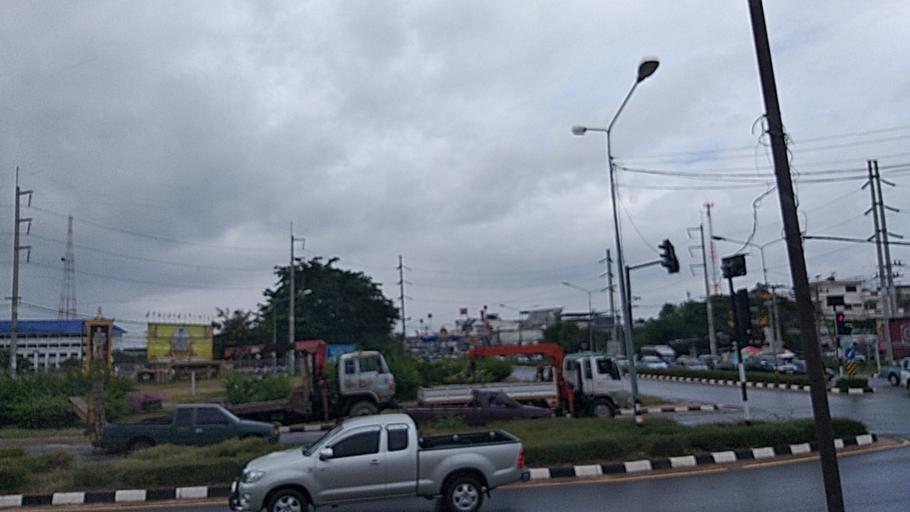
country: TH
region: Maha Sarakham
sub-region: Amphoe Borabue
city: Borabue
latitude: 16.0443
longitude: 103.1240
